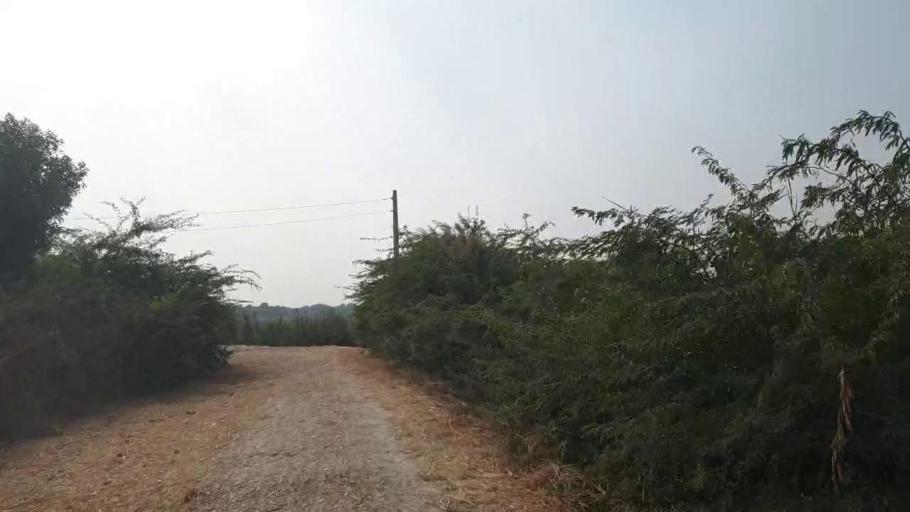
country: PK
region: Sindh
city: Rajo Khanani
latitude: 25.0439
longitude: 68.8027
